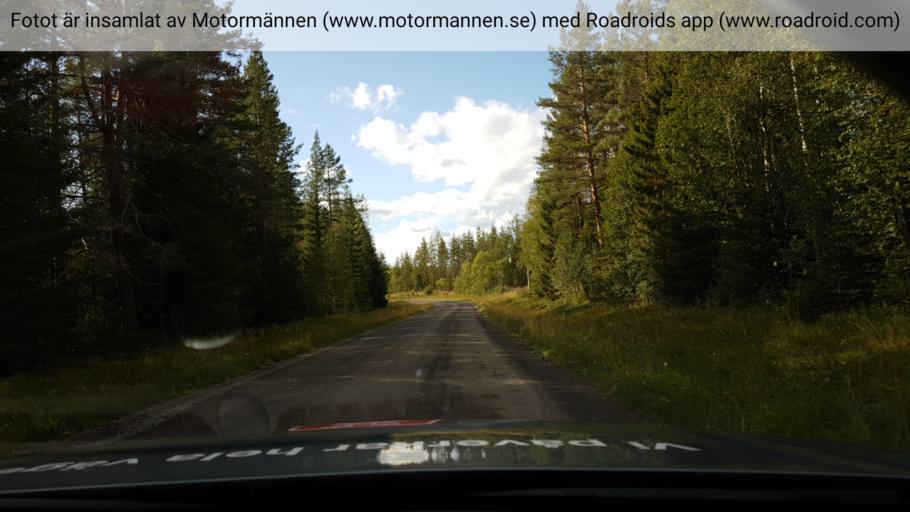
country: SE
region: Jaemtland
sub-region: OEstersunds Kommun
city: Lit
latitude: 63.3227
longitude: 15.2154
